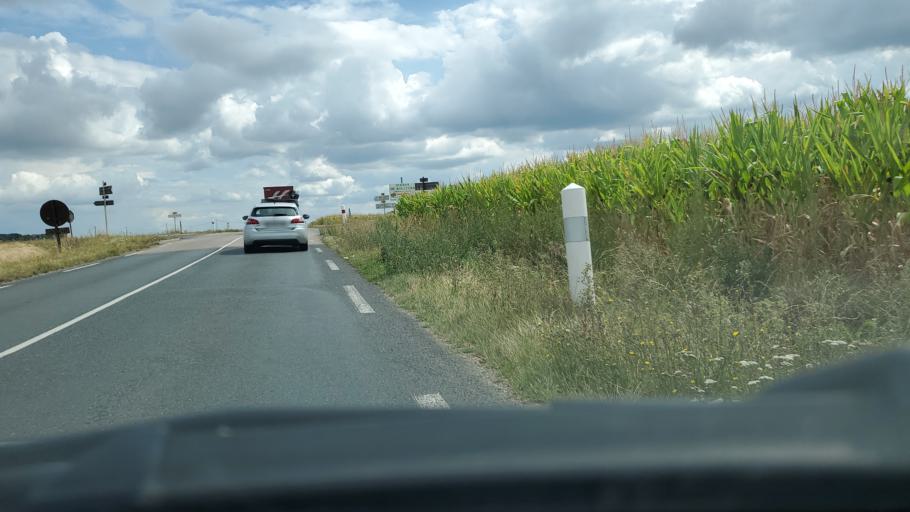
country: FR
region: Ile-de-France
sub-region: Departement de Seine-et-Marne
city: Bouleurs
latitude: 48.8958
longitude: 2.9406
